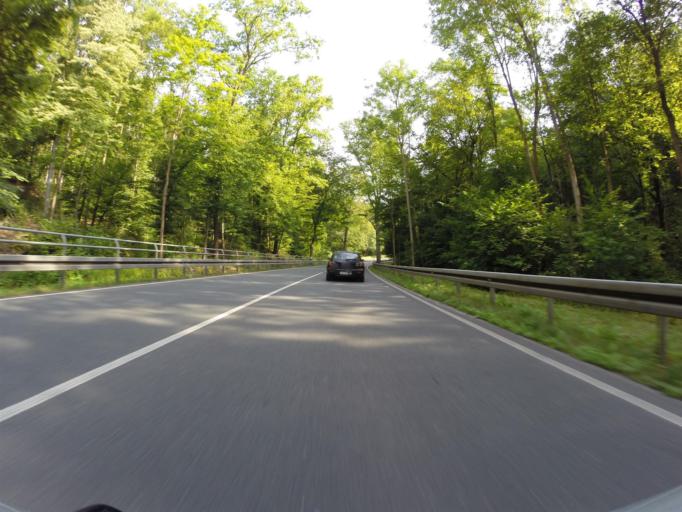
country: DE
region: Thuringia
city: Grossschwabhausen
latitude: 50.9465
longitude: 11.5327
